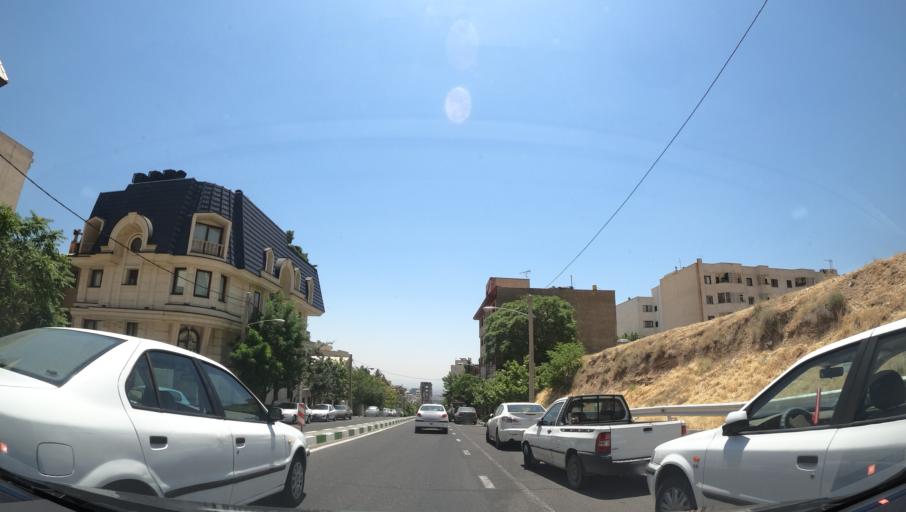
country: IR
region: Tehran
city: Tajrish
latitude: 35.8117
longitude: 51.3992
